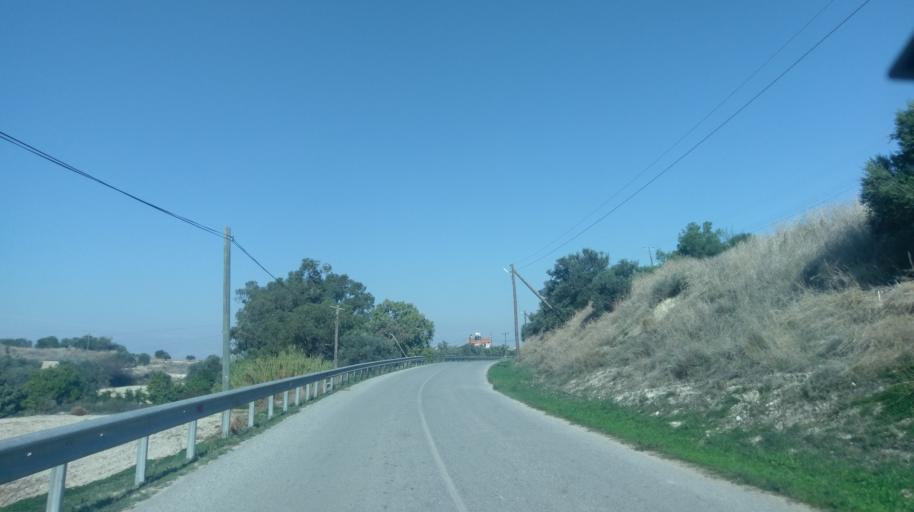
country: CY
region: Lefkosia
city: Lympia
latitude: 35.0187
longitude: 33.4661
